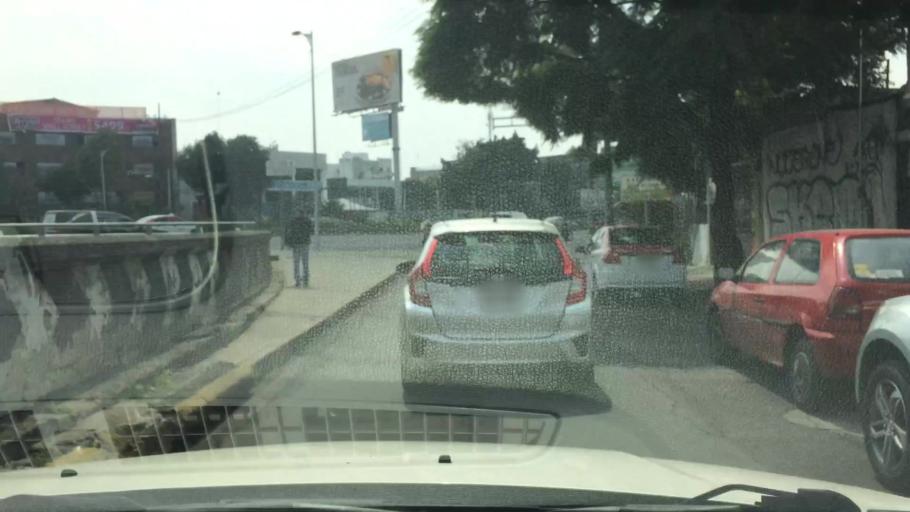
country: MX
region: Mexico City
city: Colonia Nativitas
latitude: 19.3773
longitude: -99.1411
